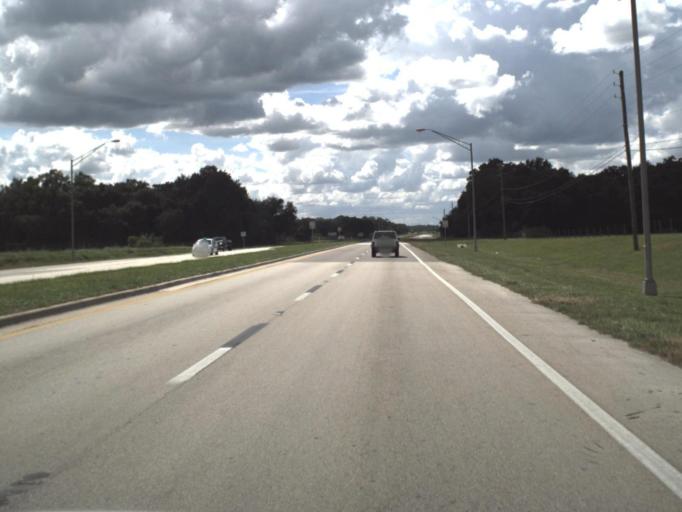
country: US
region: Florida
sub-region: Polk County
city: Jan-Phyl Village
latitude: 28.0104
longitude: -81.8217
